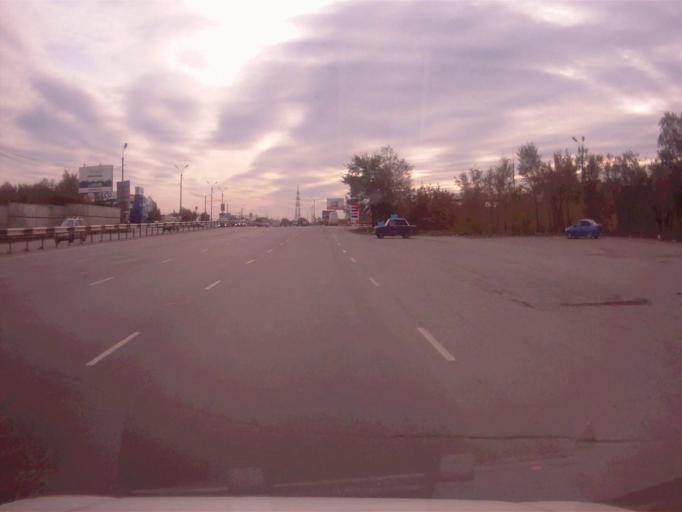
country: RU
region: Chelyabinsk
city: Novosineglazovskiy
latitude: 55.0770
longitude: 61.3881
